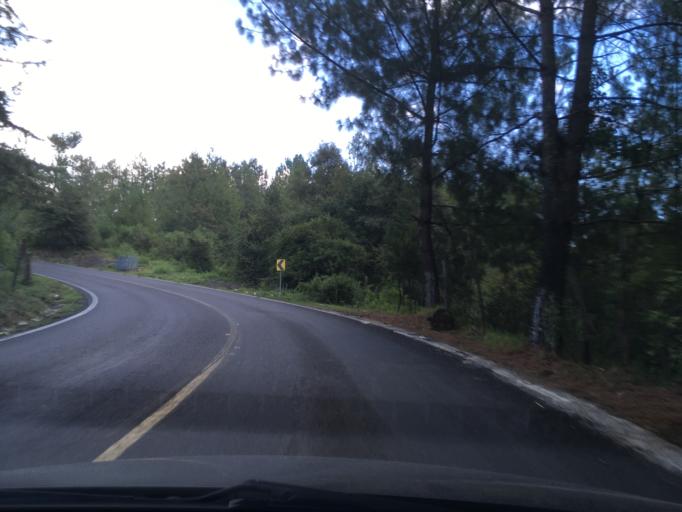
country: MX
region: Michoacan
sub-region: Nahuatzen
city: Sevina
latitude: 19.6299
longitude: -101.8954
